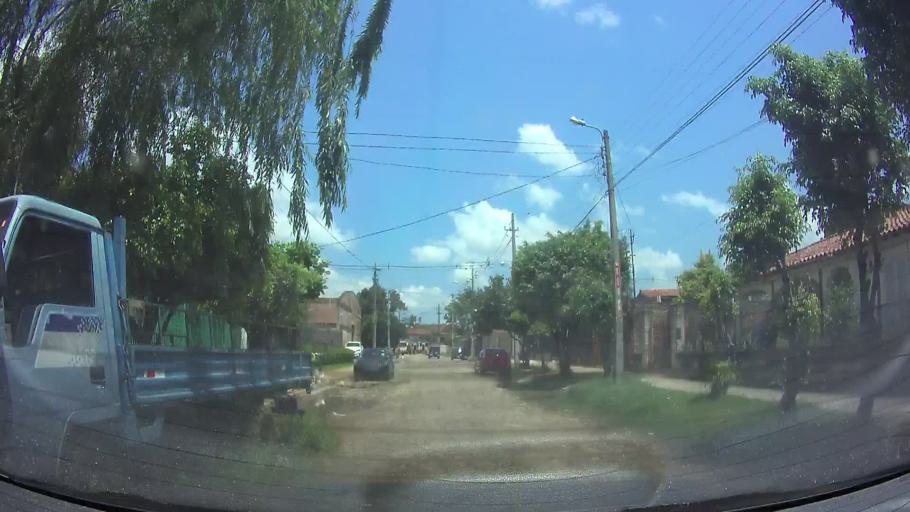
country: PY
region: Central
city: Fernando de la Mora
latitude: -25.3023
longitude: -57.5502
